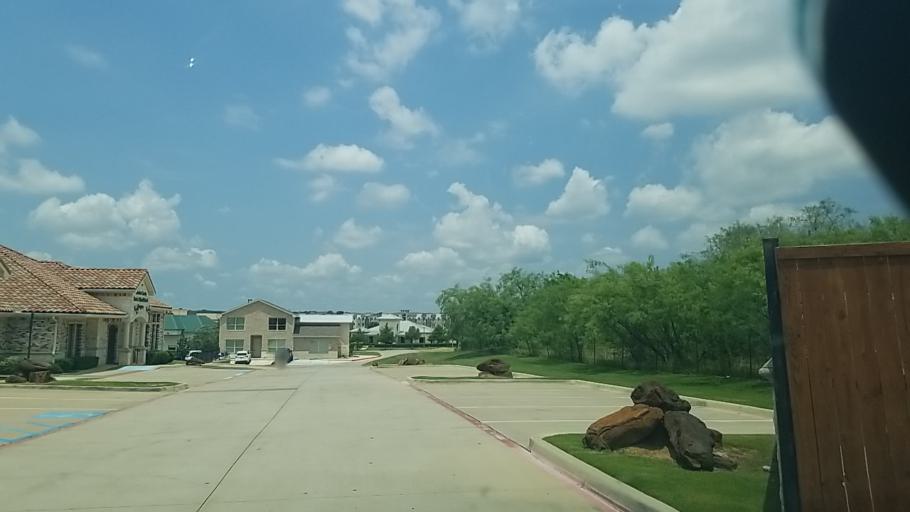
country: US
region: Texas
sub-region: Denton County
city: Corinth
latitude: 33.1745
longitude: -97.0952
